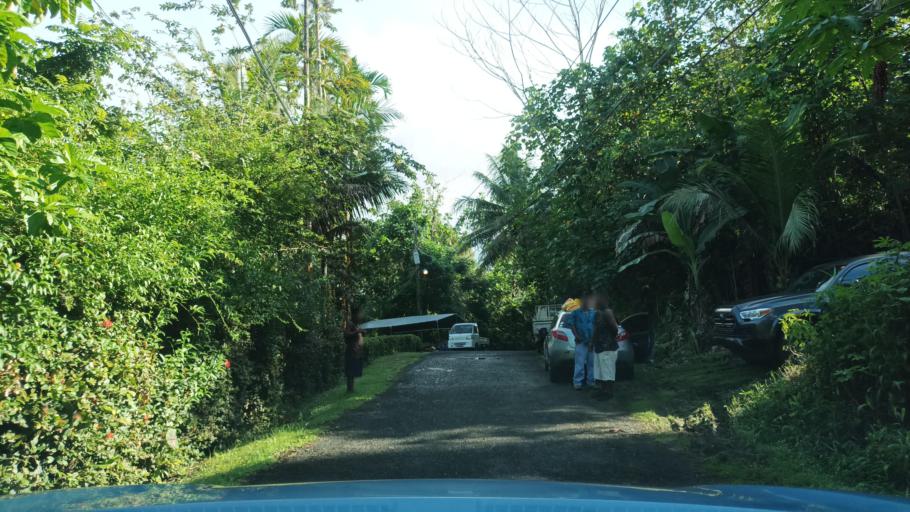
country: FM
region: Pohnpei
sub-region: Kolonia Municipality
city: Kolonia Town
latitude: 6.9591
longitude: 158.1951
